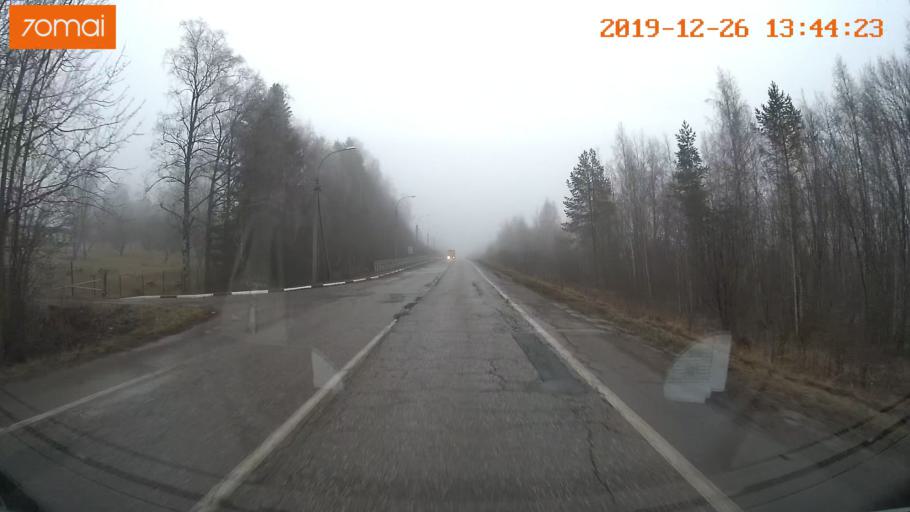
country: RU
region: Vologda
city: Sheksna
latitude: 58.7023
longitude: 38.5058
